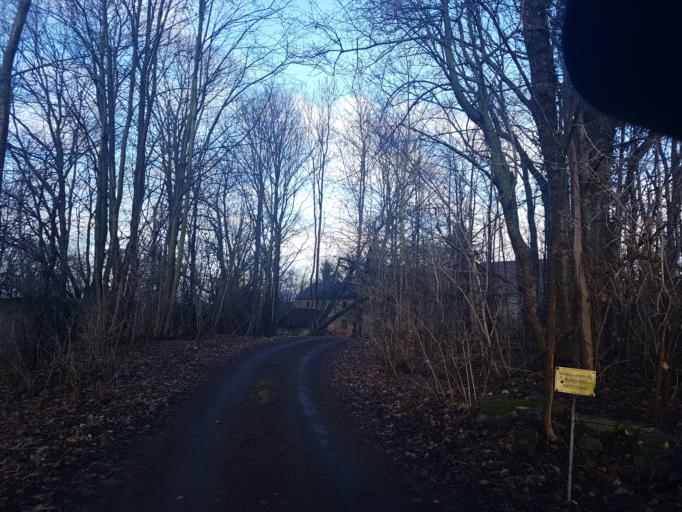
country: DE
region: Brandenburg
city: Ruckersdorf
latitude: 51.5991
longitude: 13.6244
